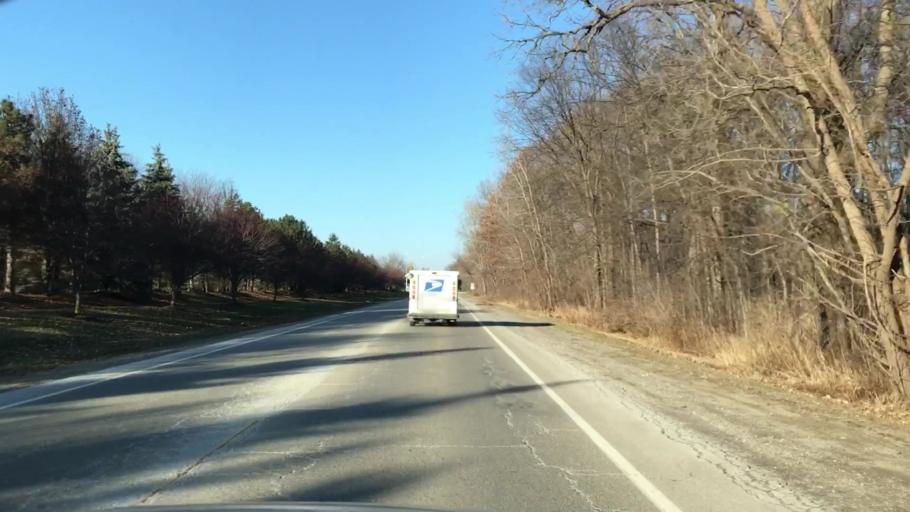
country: US
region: Michigan
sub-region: Oakland County
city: Novi
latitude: 42.4690
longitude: -83.5144
